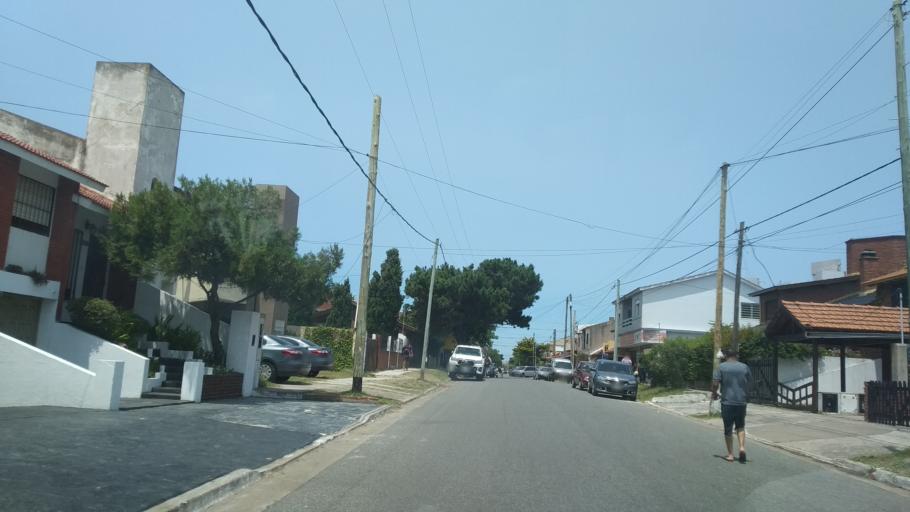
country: AR
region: Buenos Aires
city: Mar del Tuyu
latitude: -36.5581
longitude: -56.6895
